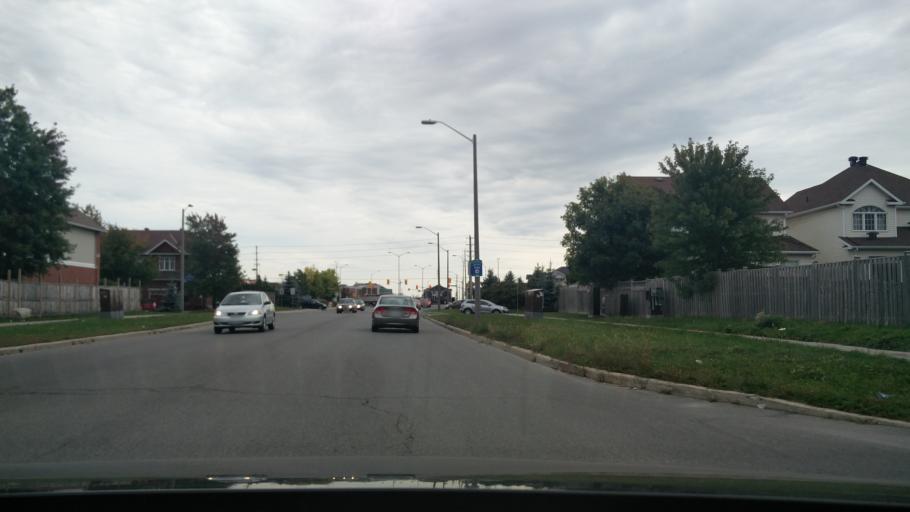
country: CA
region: Ontario
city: Bells Corners
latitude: 45.2756
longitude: -75.7399
